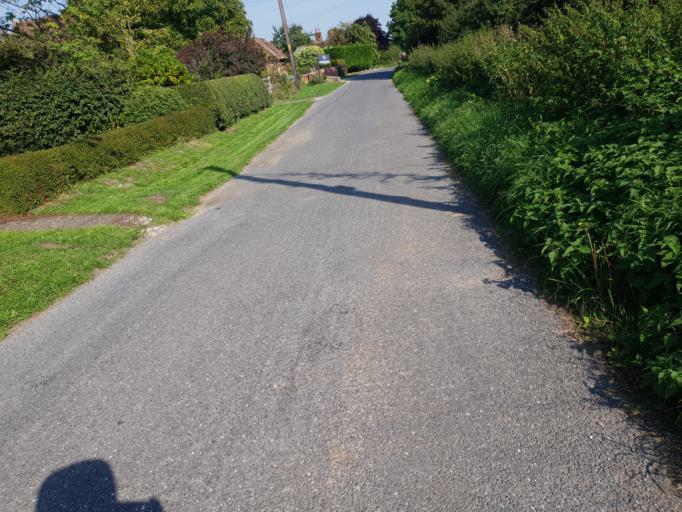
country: GB
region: England
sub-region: Suffolk
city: East Bergholt
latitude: 51.9502
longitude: 0.9992
